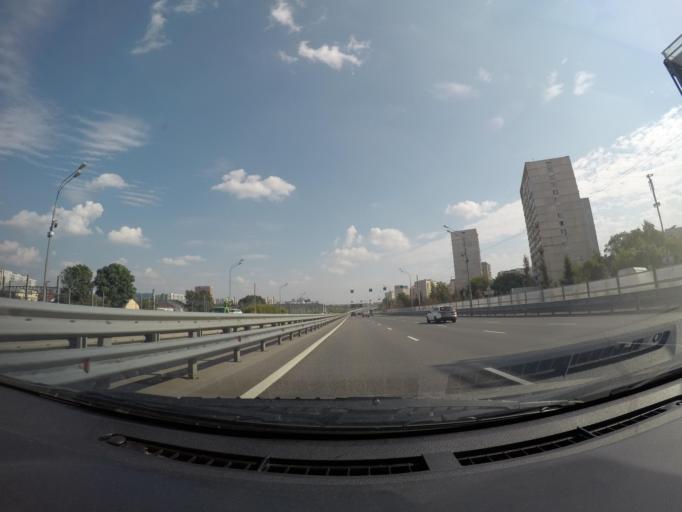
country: RU
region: Moskovskaya
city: Levoberezhnaya
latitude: 55.8776
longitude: 37.4895
